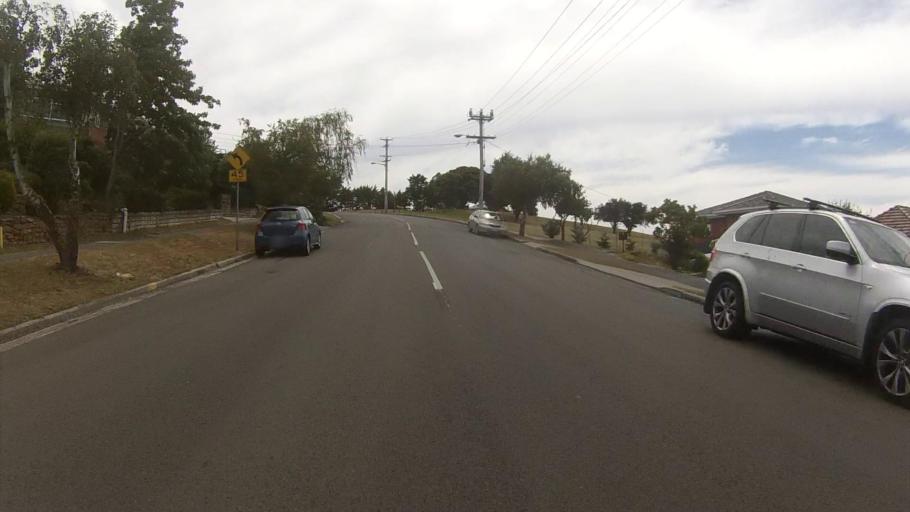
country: AU
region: Tasmania
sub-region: Kingborough
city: Taroona
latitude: -42.9166
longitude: 147.3579
